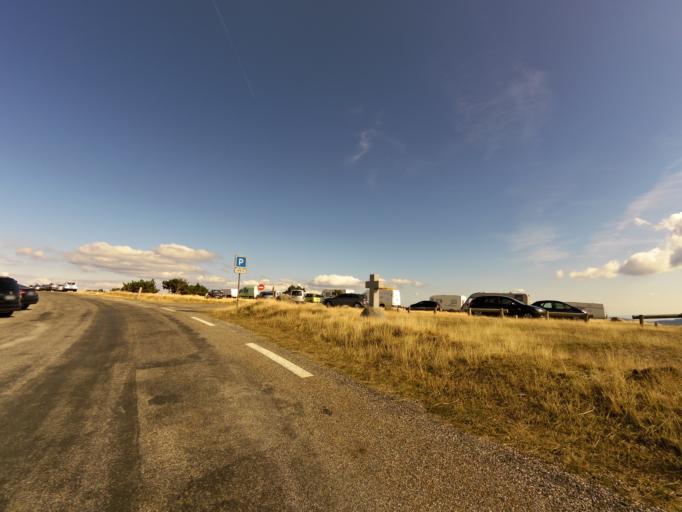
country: FR
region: Languedoc-Roussillon
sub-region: Departement du Gard
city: Valleraugue
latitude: 44.1214
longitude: 3.5774
